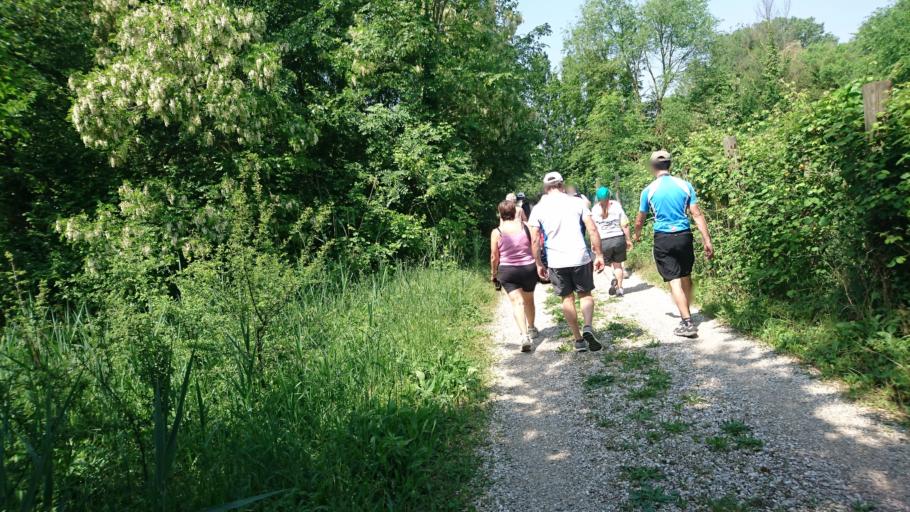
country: IT
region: Veneto
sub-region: Provincia di Venezia
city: Campagna Lupia
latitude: 45.3622
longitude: 12.1383
